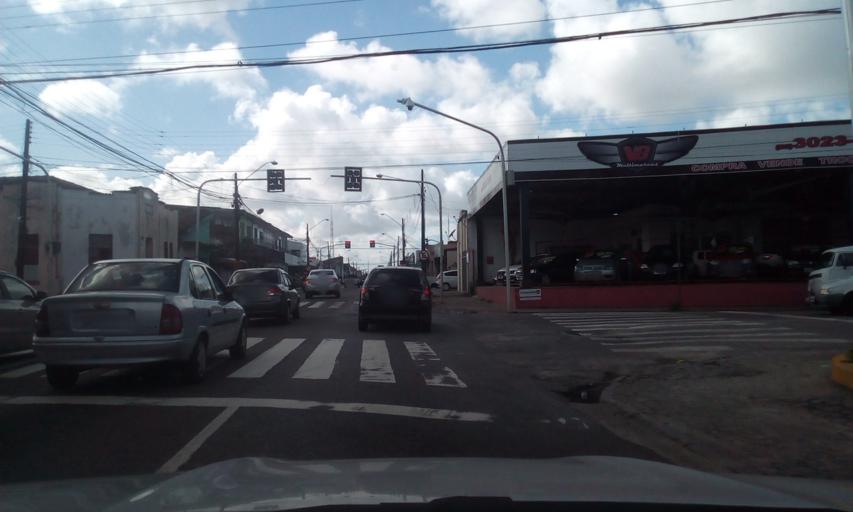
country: BR
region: Paraiba
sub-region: Joao Pessoa
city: Joao Pessoa
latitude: -7.1332
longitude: -34.8788
